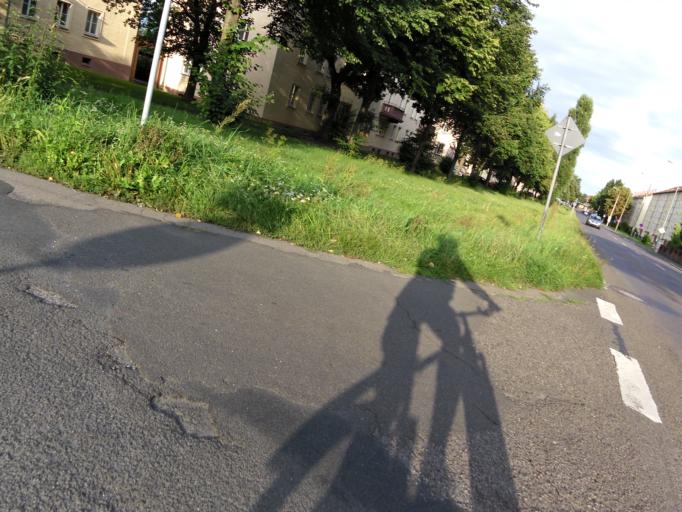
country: DE
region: Saxony
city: Leipzig
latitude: 51.3757
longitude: 12.4069
